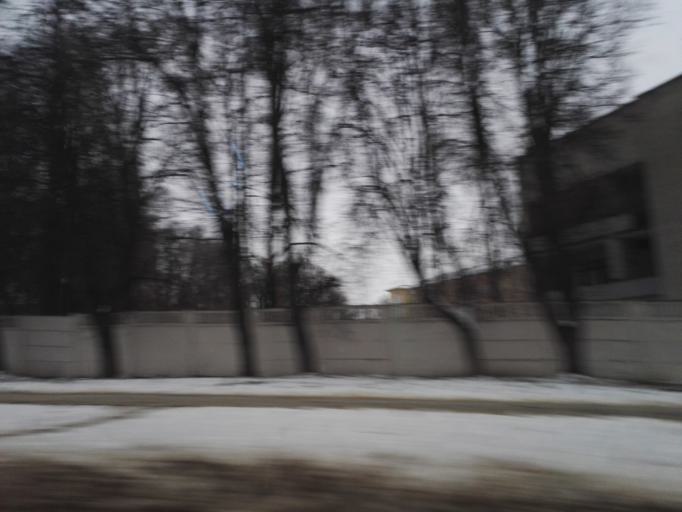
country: RU
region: Tula
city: Novomoskovsk
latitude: 54.0180
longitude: 38.3044
